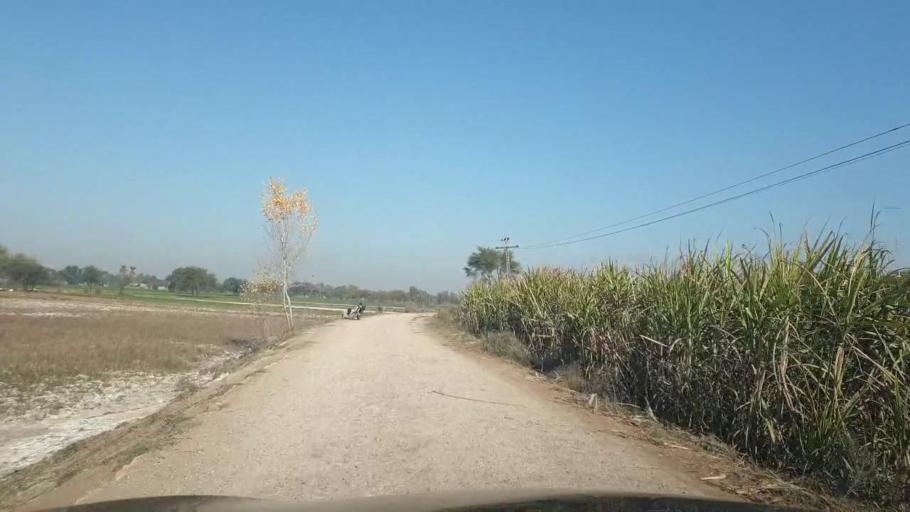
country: PK
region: Sindh
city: Ghotki
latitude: 27.9973
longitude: 69.3421
